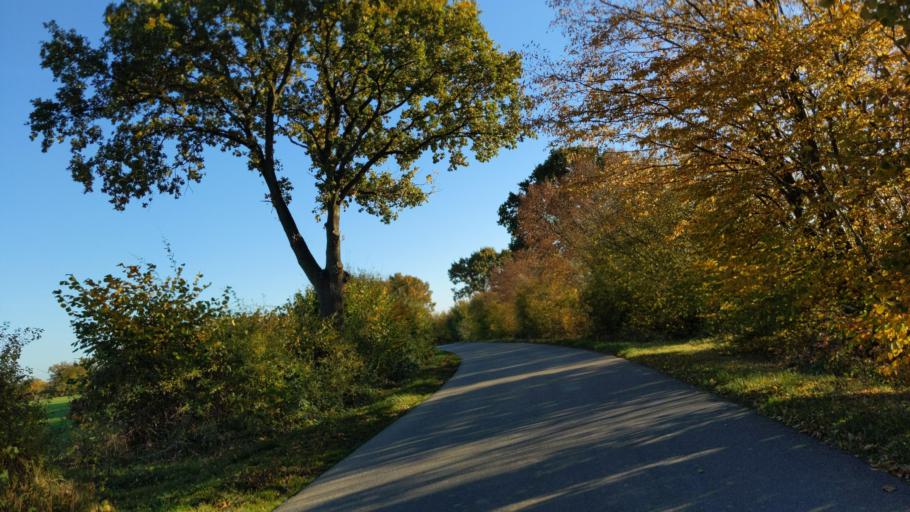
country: DE
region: Schleswig-Holstein
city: Einhaus
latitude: 53.7250
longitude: 10.7194
